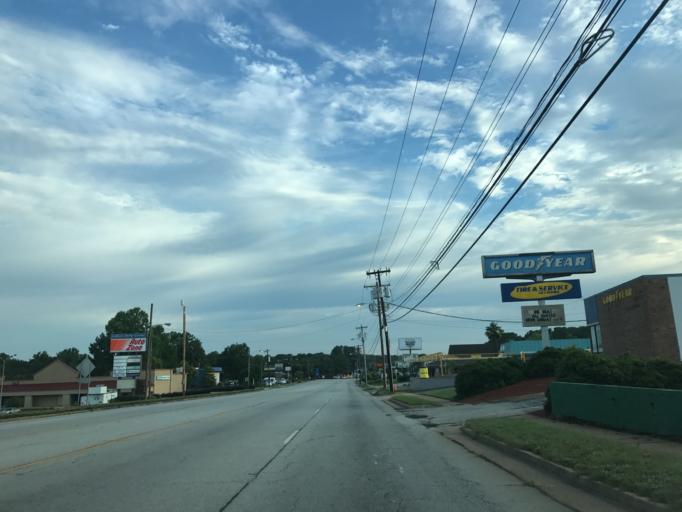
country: US
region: South Carolina
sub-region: Greenville County
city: Mauldin
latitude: 34.7836
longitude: -82.3121
